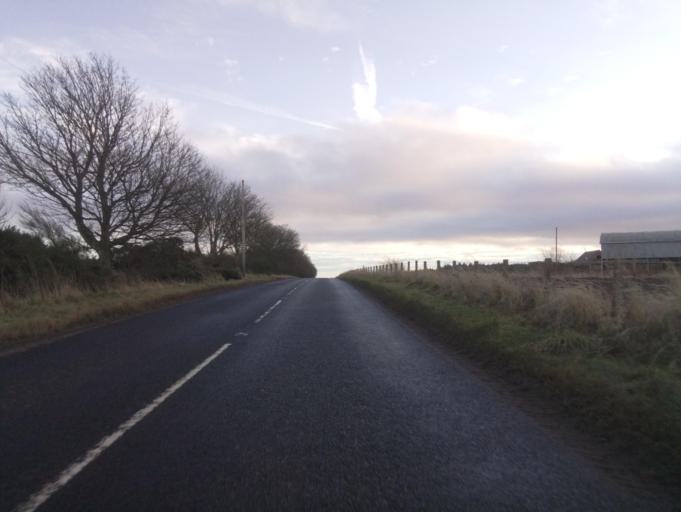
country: GB
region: Scotland
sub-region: Angus
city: Letham
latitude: 56.5628
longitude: -2.7726
